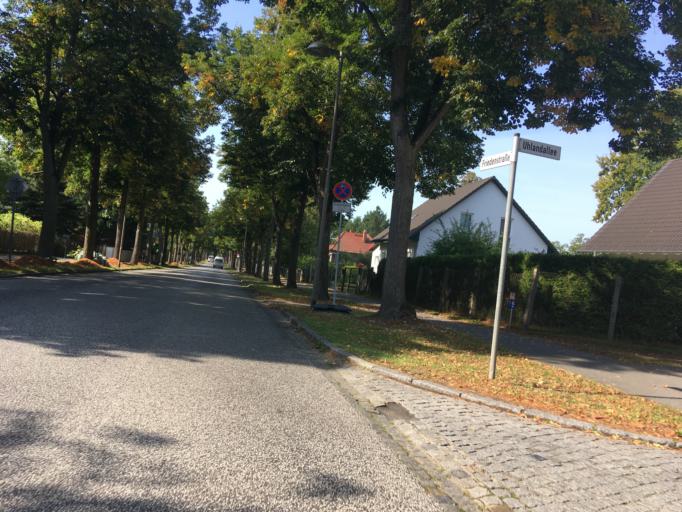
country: DE
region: Brandenburg
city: Zeuthen
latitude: 52.3685
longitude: 13.6294
